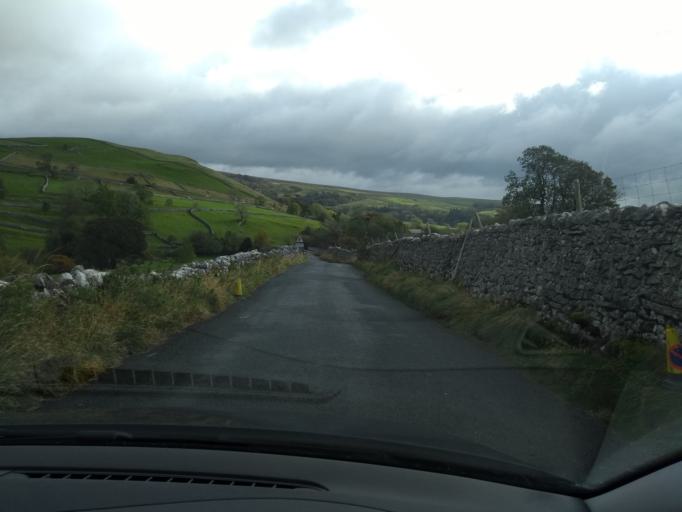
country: GB
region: England
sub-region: North Yorkshire
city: Gargrave
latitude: 54.0662
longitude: -2.1590
